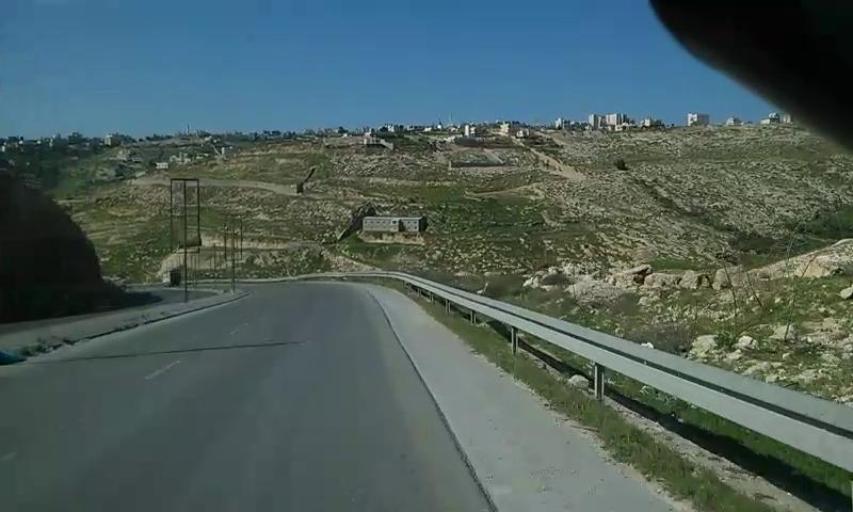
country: PS
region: West Bank
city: Abu Dis
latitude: 31.7506
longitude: 35.2781
